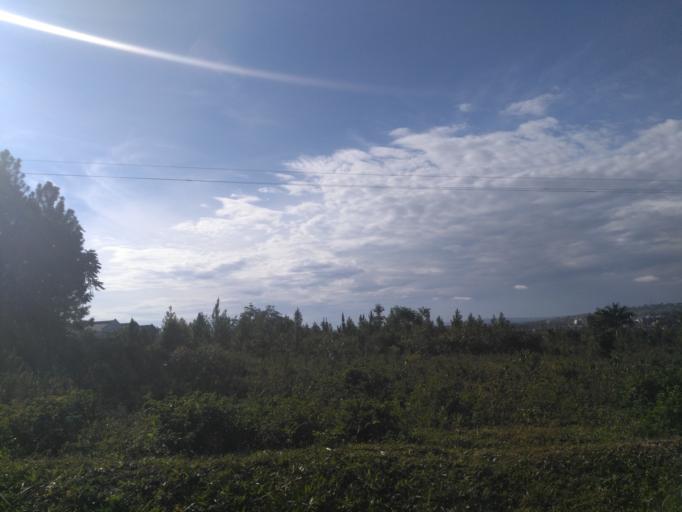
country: UG
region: Eastern Region
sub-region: Jinja District
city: Jinja
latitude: 0.4573
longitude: 33.1810
